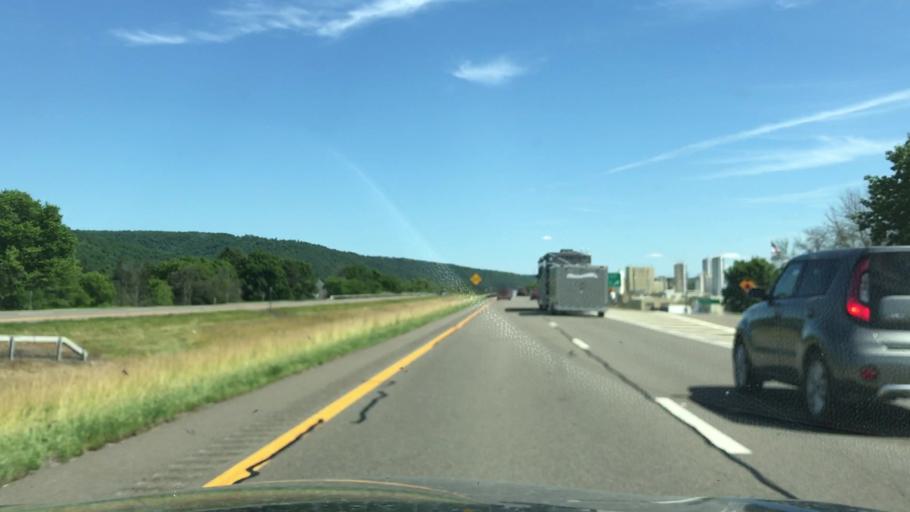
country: US
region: New York
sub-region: Steuben County
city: Gang Mills
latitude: 42.2307
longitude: -77.1883
